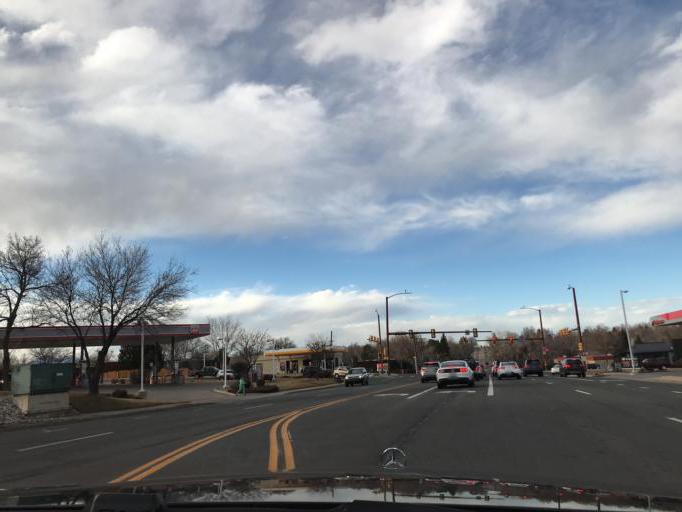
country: US
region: Colorado
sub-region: Jefferson County
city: Arvada
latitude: 39.8117
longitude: -105.1379
